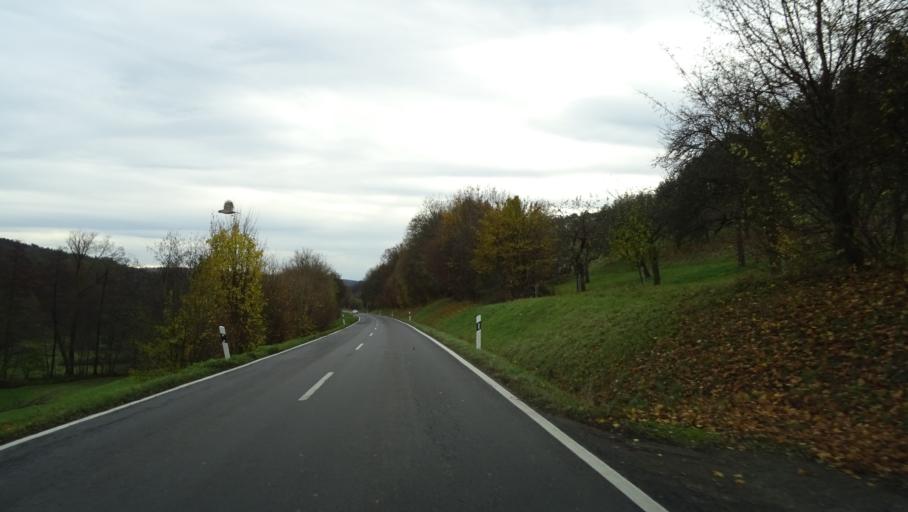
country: DE
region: Baden-Wuerttemberg
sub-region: Karlsruhe Region
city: Mosbach
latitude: 49.3666
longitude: 9.1263
